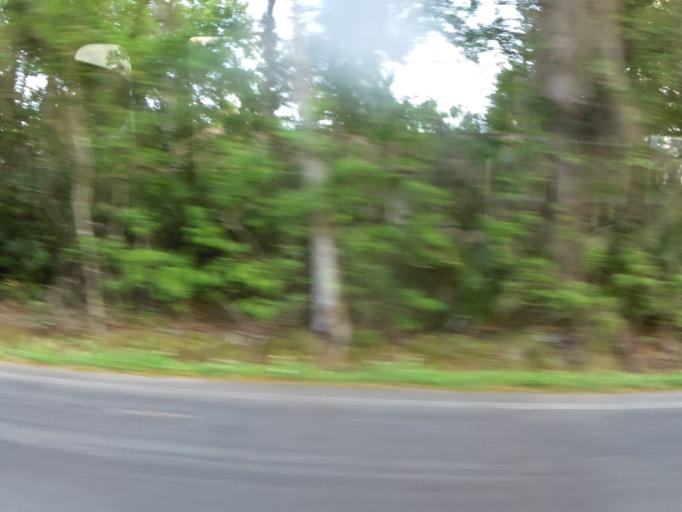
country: US
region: Florida
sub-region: Saint Johns County
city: Fruit Cove
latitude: 30.1290
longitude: -81.6199
